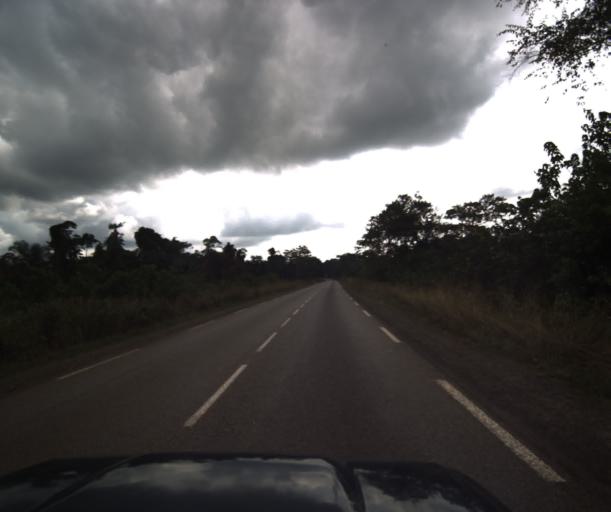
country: CM
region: Littoral
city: Edea
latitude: 3.8127
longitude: 10.3068
